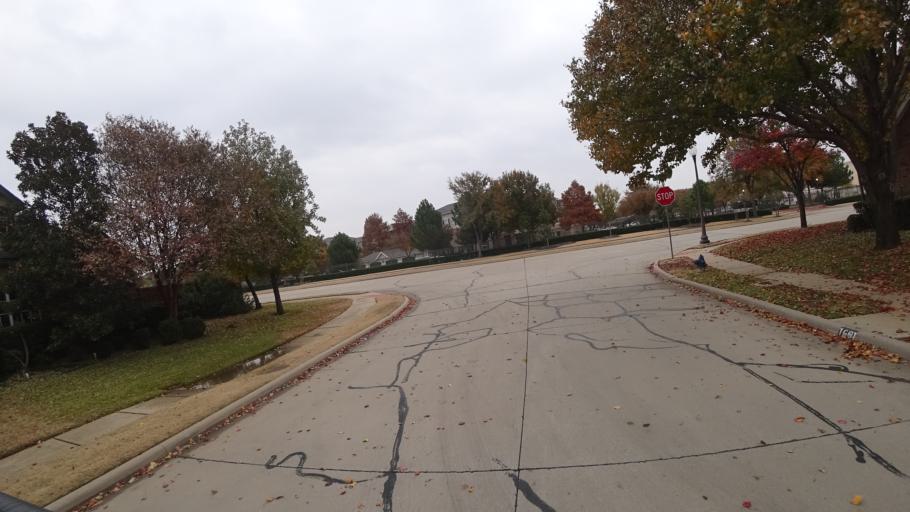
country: US
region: Texas
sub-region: Denton County
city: Lewisville
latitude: 33.0272
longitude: -96.9347
